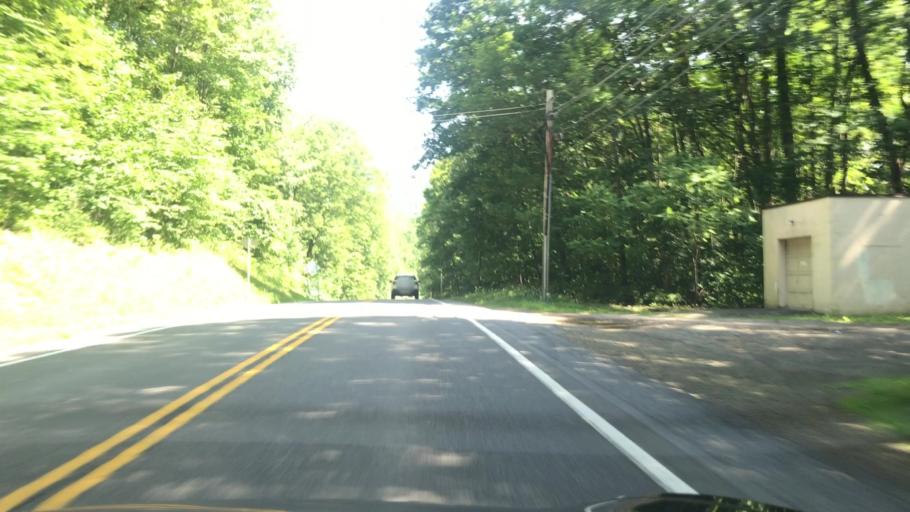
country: US
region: Pennsylvania
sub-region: Tioga County
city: Blossburg
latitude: 41.4788
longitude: -76.9803
